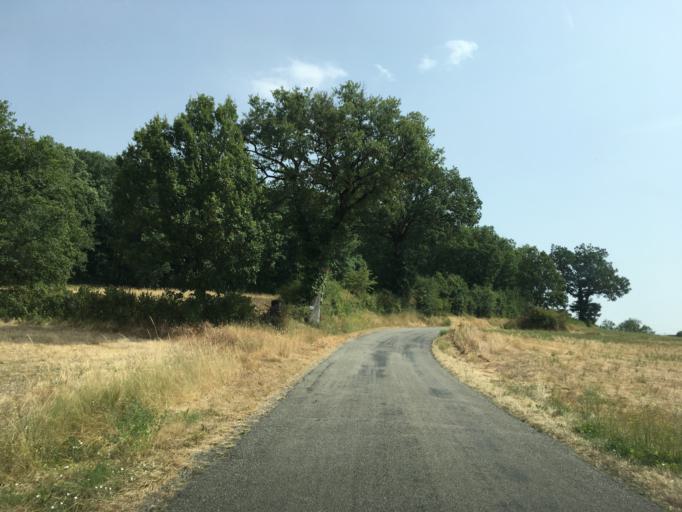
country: FR
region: Midi-Pyrenees
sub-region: Departement du Lot
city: Le Vigan
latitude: 44.7468
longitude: 1.4953
